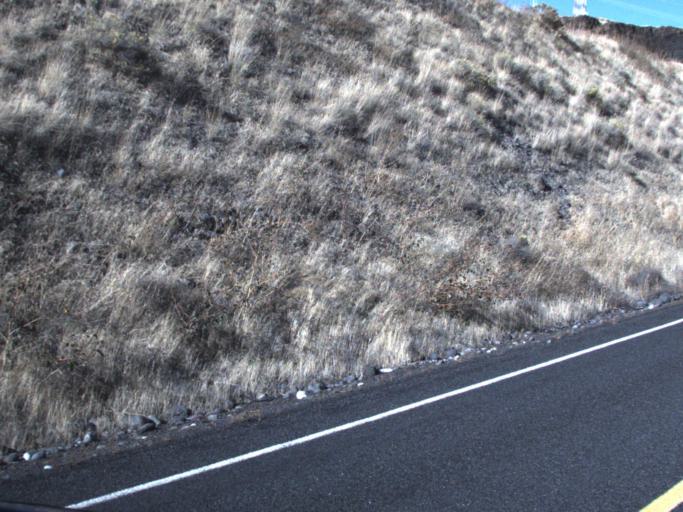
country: US
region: Washington
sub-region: Franklin County
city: Connell
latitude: 46.5412
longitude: -118.5612
